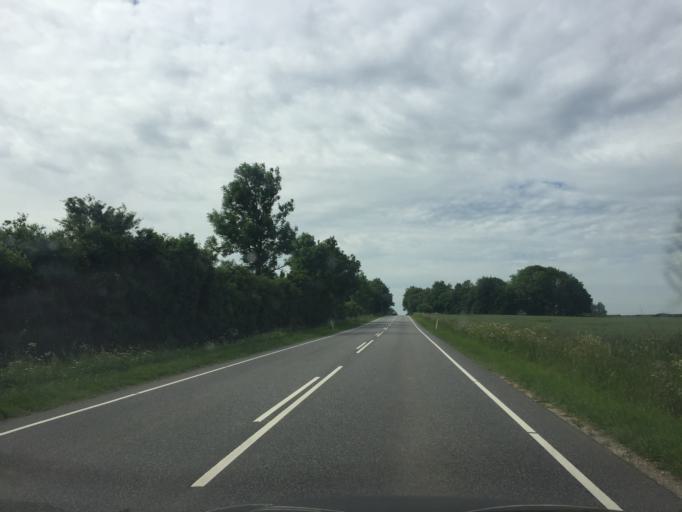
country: DK
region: South Denmark
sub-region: Faaborg-Midtfyn Kommune
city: Ringe
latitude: 55.2089
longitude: 10.5696
